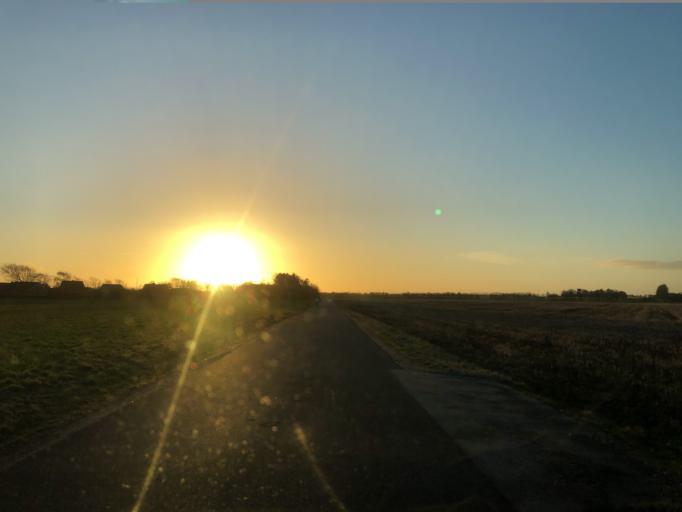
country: DK
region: Central Jutland
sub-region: Skive Kommune
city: Skive
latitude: 56.5353
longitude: 8.9306
